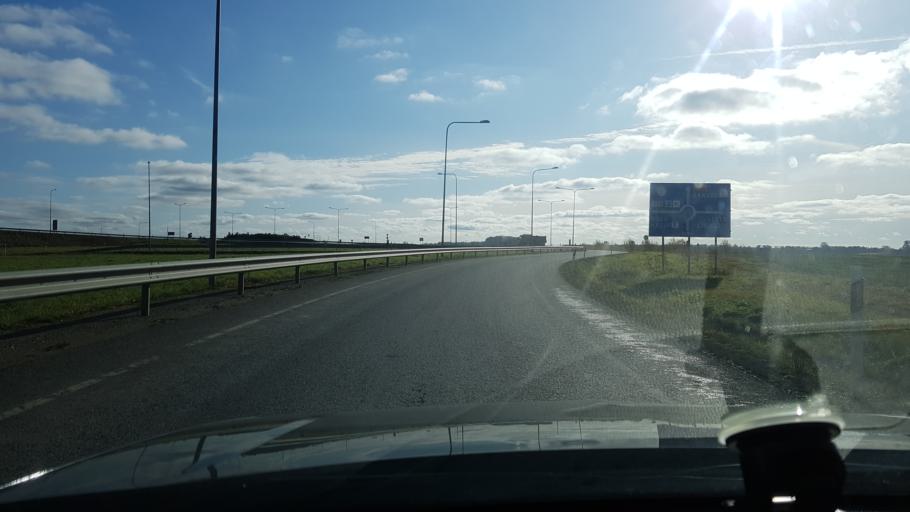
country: EE
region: Laeaene-Virumaa
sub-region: Haljala vald
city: Haljala
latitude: 59.4240
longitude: 26.2661
